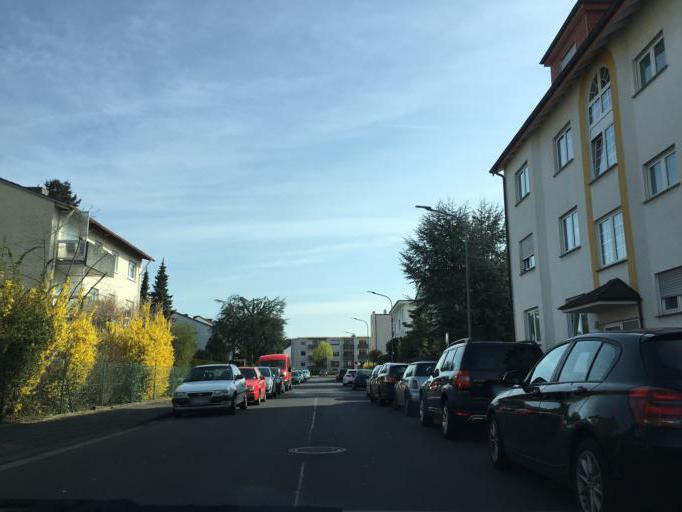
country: DE
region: Hesse
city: Obertshausen
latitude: 50.0671
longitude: 8.8419
